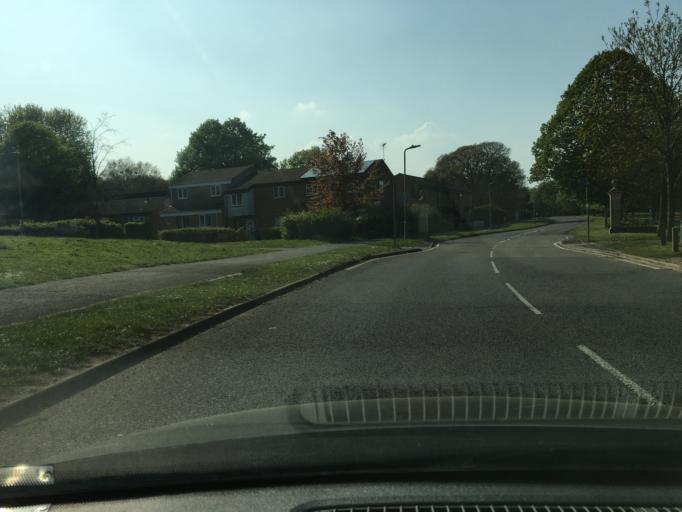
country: GB
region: England
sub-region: Bracknell Forest
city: Bracknell
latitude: 51.3943
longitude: -0.7517
